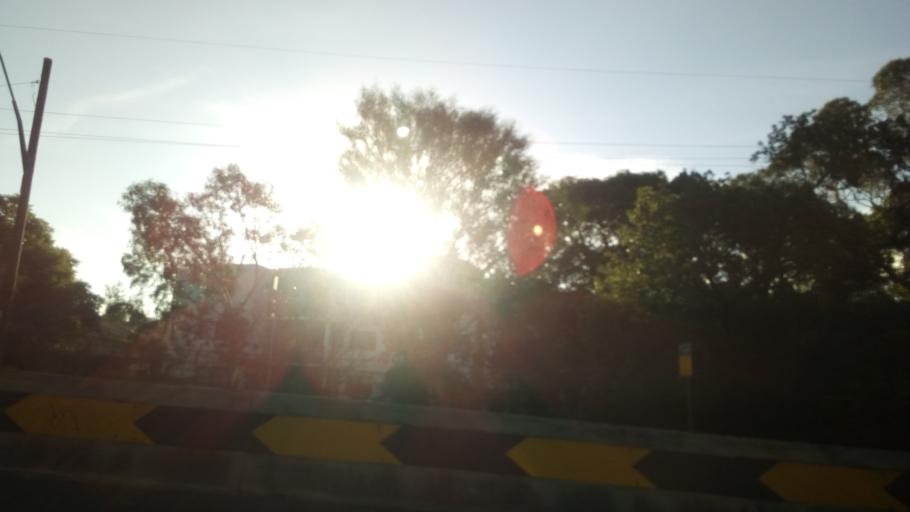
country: AU
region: New South Wales
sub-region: Kogarah
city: Blakehurst
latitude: -34.0083
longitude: 151.1112
